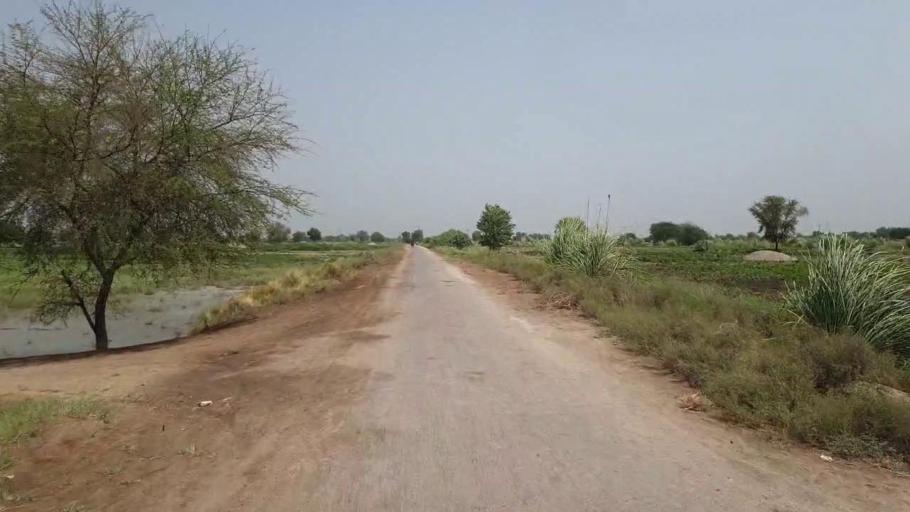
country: PK
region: Sindh
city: Nawabshah
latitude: 26.2647
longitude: 68.3175
